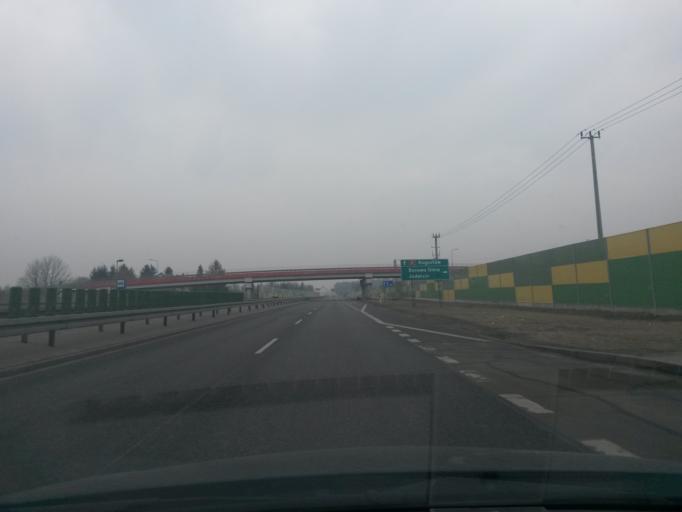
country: PL
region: Masovian Voivodeship
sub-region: Powiat legionowski
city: Serock
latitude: 52.4821
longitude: 21.0396
